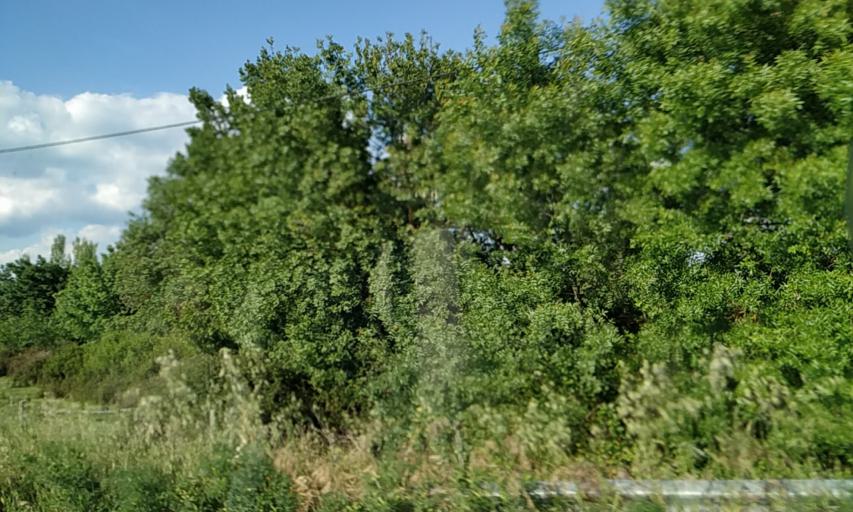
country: PT
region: Portalegre
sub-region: Portalegre
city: Urra
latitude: 39.1259
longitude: -7.4464
